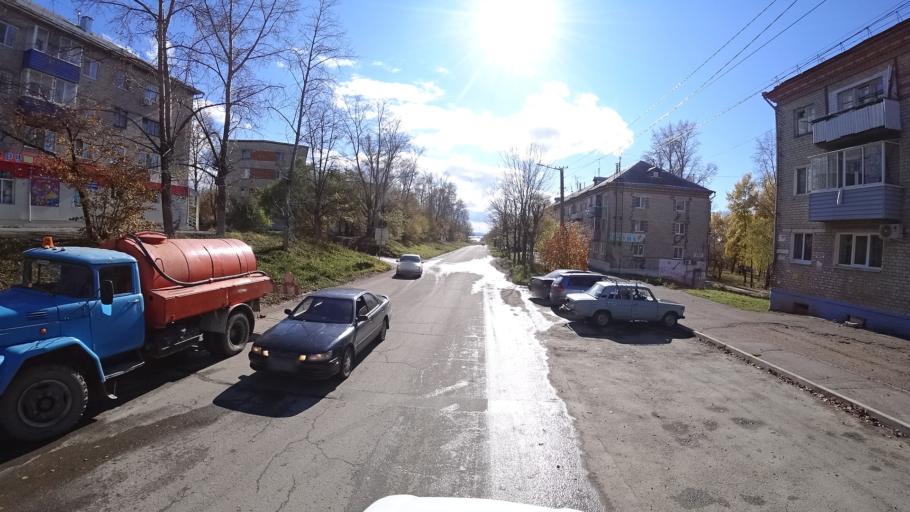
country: RU
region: Khabarovsk Krai
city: Amursk
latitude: 50.2183
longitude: 136.9032
